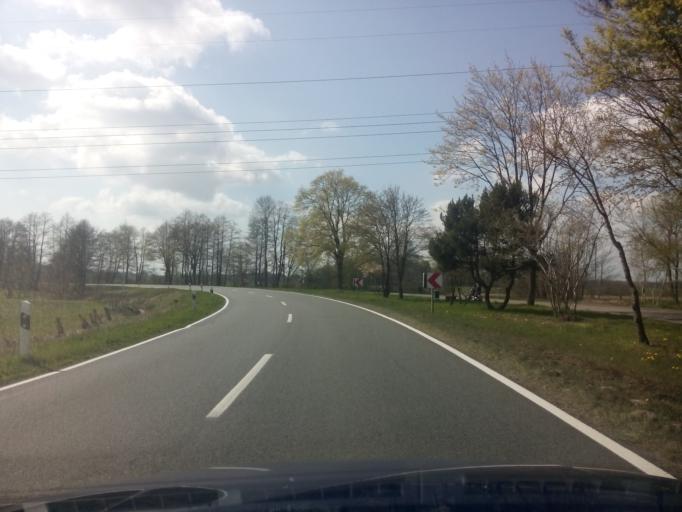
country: DE
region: Lower Saxony
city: Lilienthal
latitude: 53.1818
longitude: 8.8742
